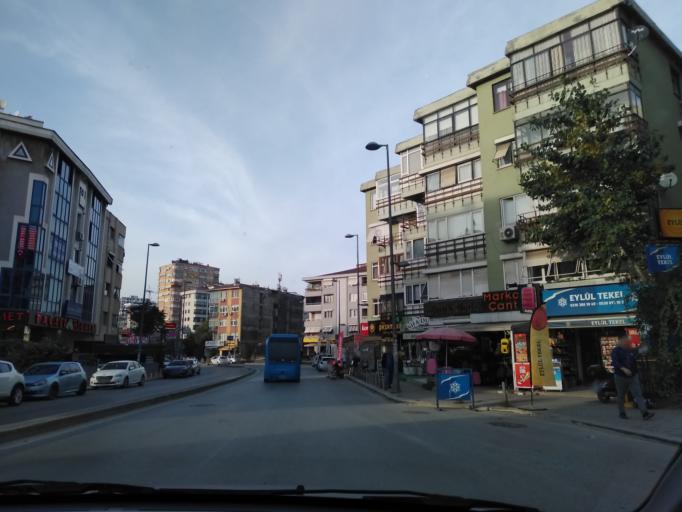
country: TR
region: Istanbul
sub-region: Atasehir
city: Atasehir
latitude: 40.9544
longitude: 29.1008
